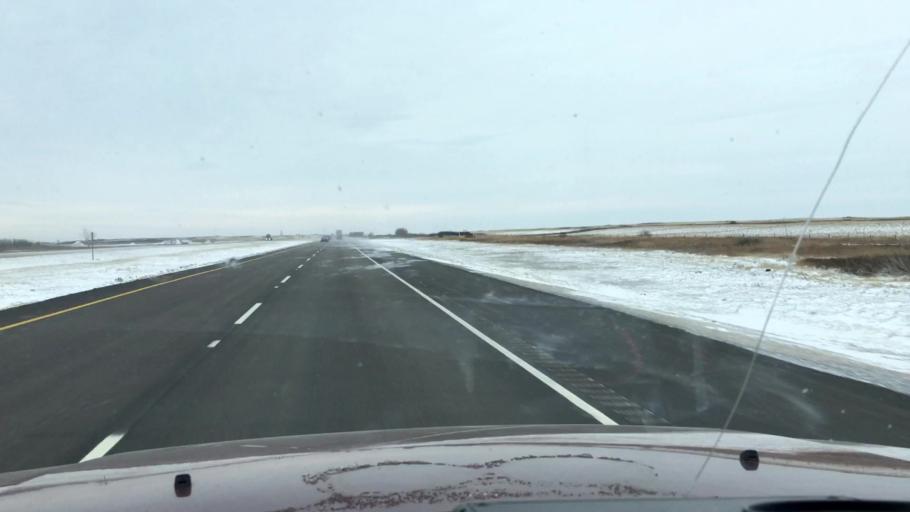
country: CA
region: Saskatchewan
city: Moose Jaw
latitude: 50.8953
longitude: -105.6294
